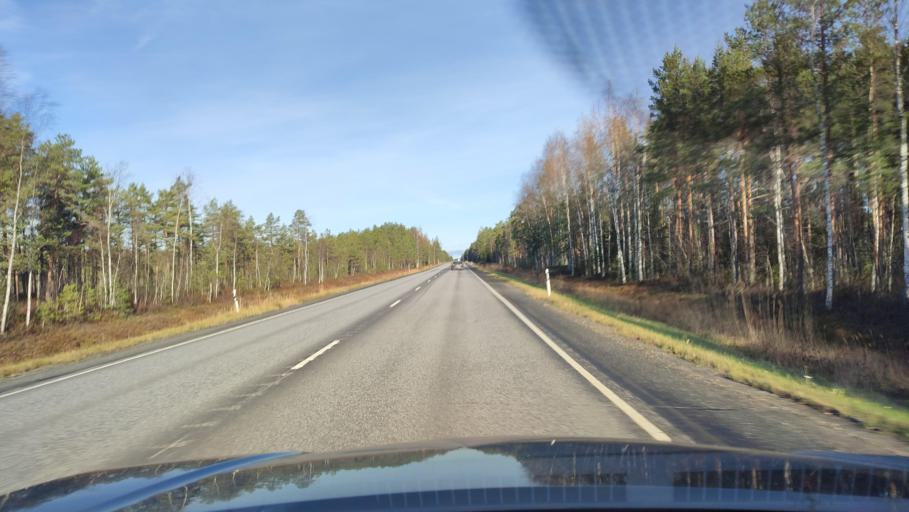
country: FI
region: Ostrobothnia
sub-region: Vaasa
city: Malax
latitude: 62.7910
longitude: 21.6706
